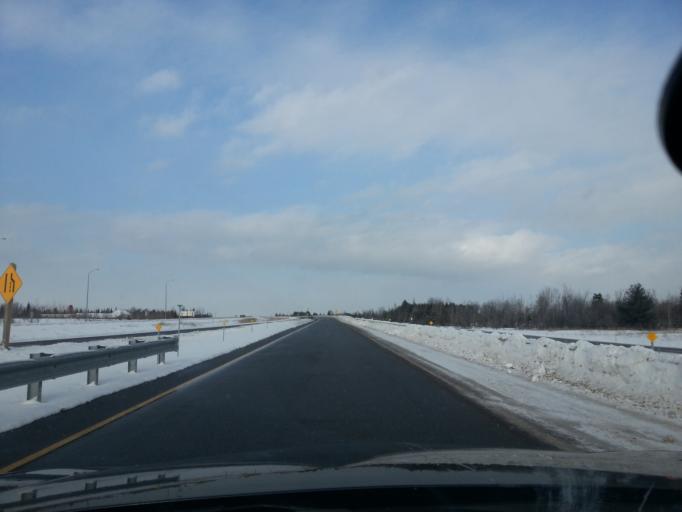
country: CA
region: Ontario
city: Carleton Place
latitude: 45.1735
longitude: -76.0479
